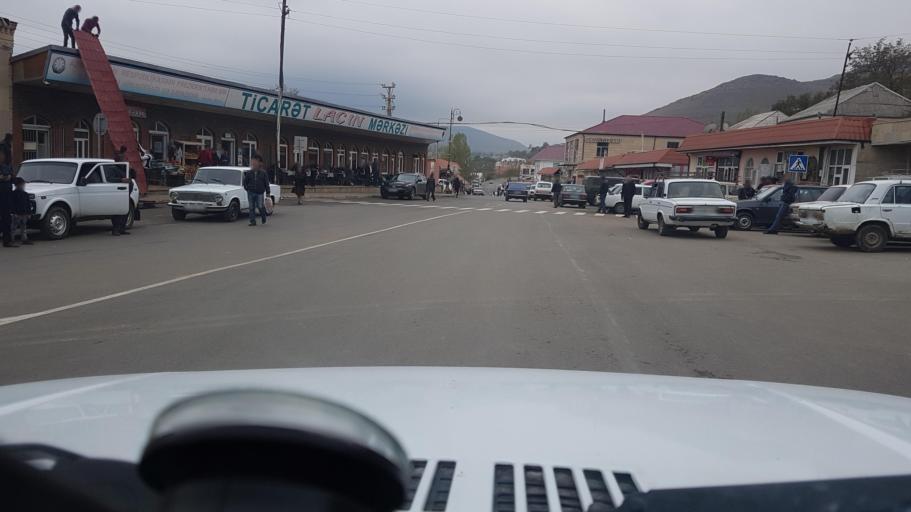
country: AZ
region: Gadabay Rayon
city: Kyadabek
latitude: 40.5744
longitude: 45.8074
